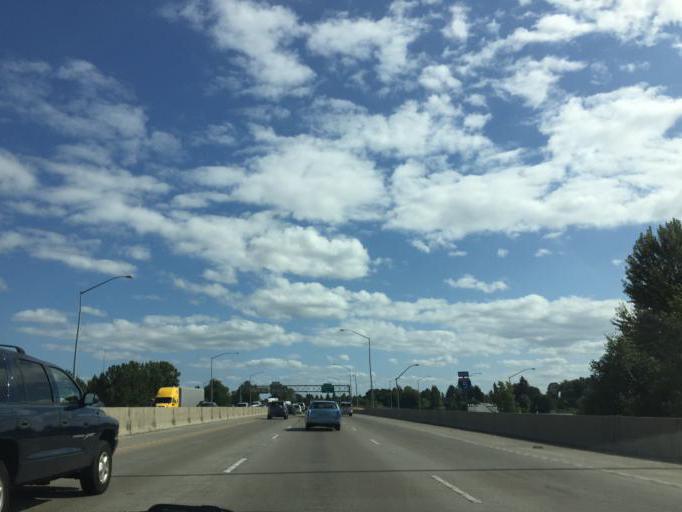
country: US
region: Washington
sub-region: Clark County
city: Vancouver
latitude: 45.5885
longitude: -122.6813
